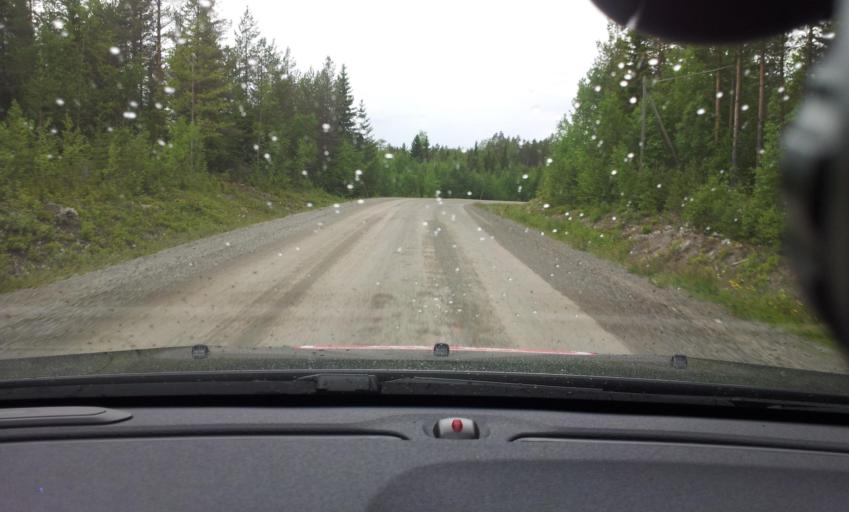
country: SE
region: Jaemtland
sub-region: OEstersunds Kommun
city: Brunflo
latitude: 63.1021
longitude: 15.0538
